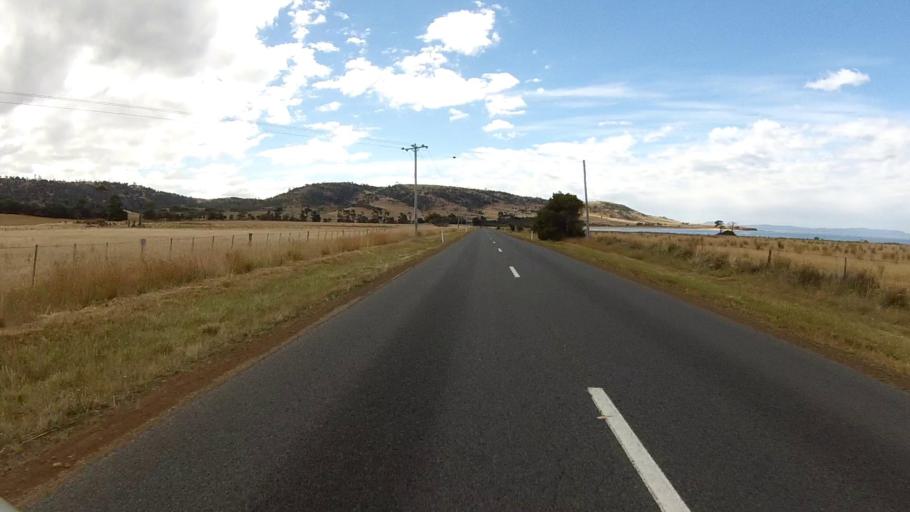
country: AU
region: Tasmania
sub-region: Sorell
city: Sorell
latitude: -42.2082
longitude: 148.0407
